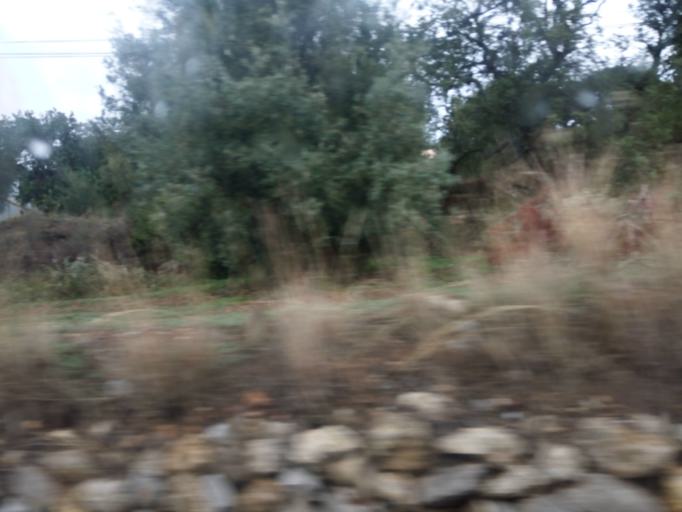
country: PT
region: Faro
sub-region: Faro
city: Santa Barbara de Nexe
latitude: 37.1053
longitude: -7.9827
